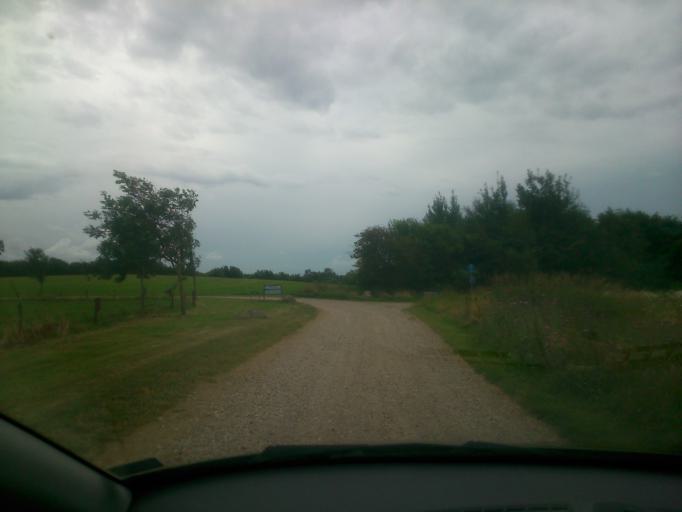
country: DK
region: South Denmark
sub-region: Esbjerg Kommune
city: Esbjerg
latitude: 55.5257
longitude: 8.4348
